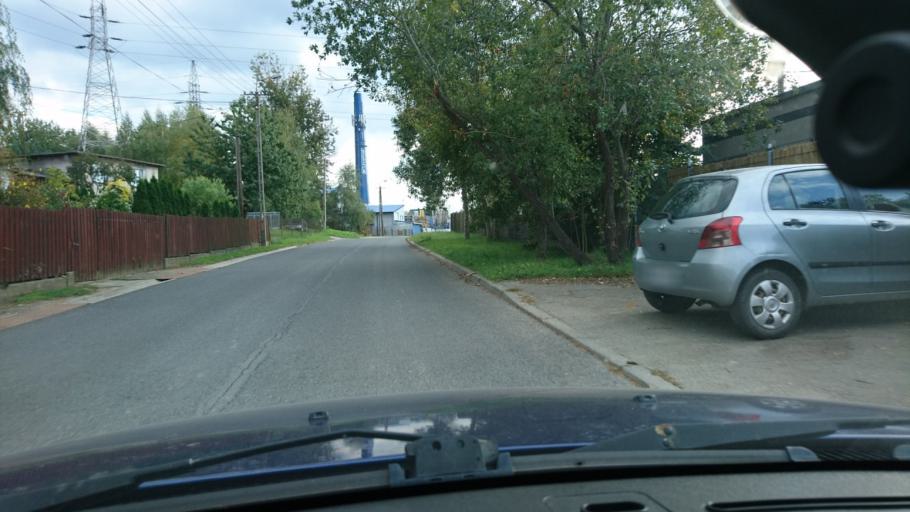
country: PL
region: Silesian Voivodeship
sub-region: Bielsko-Biala
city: Bielsko-Biala
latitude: 49.8449
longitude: 19.0553
